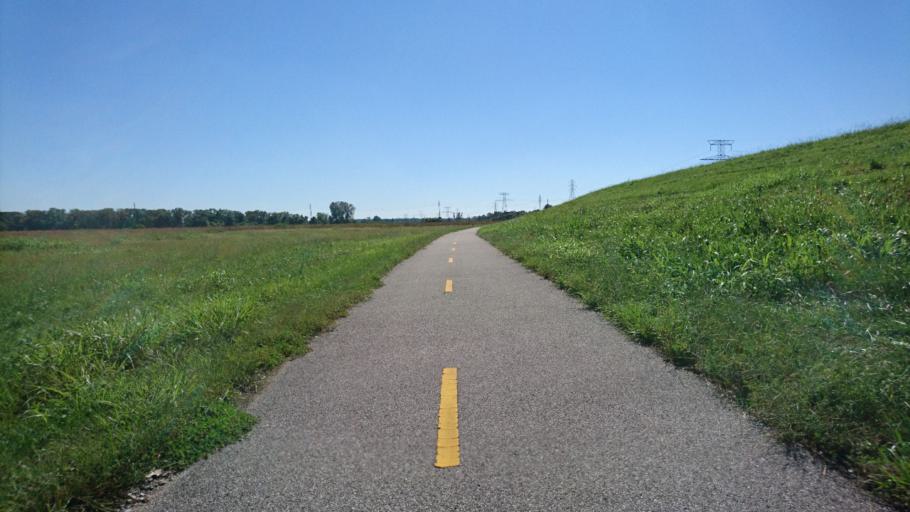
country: US
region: Illinois
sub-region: Madison County
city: Hartford
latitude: 38.8020
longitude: -90.1042
